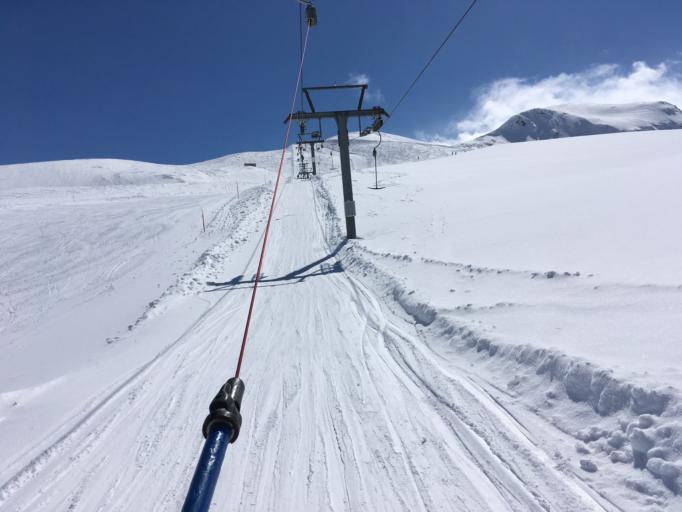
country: CH
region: Grisons
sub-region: Maloja District
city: Promontogno
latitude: 46.4396
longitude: 9.6362
